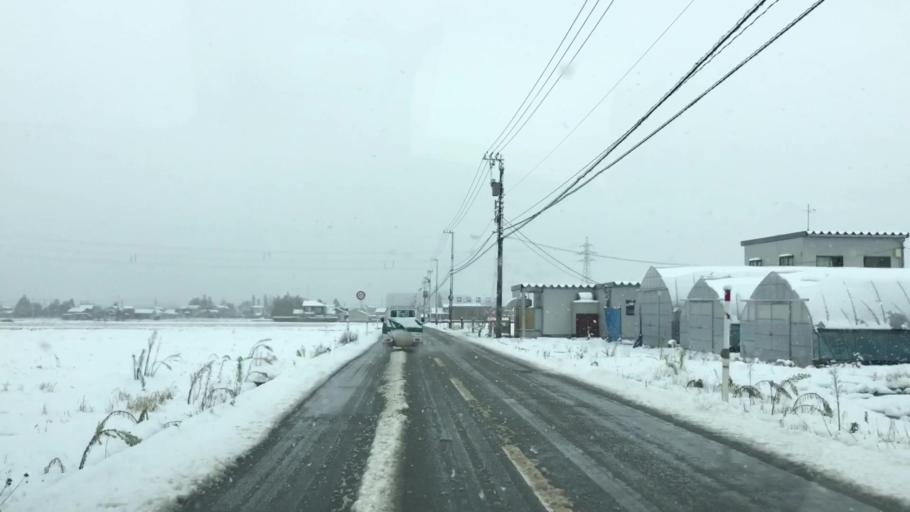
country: JP
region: Toyama
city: Kamiichi
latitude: 36.6891
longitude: 137.3364
